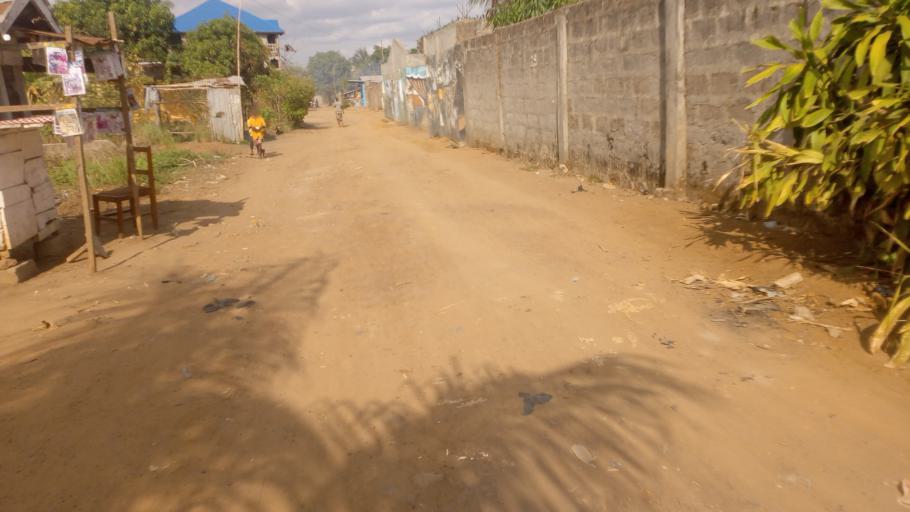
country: SL
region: Western Area
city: Waterloo
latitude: 8.3229
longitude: -13.0752
